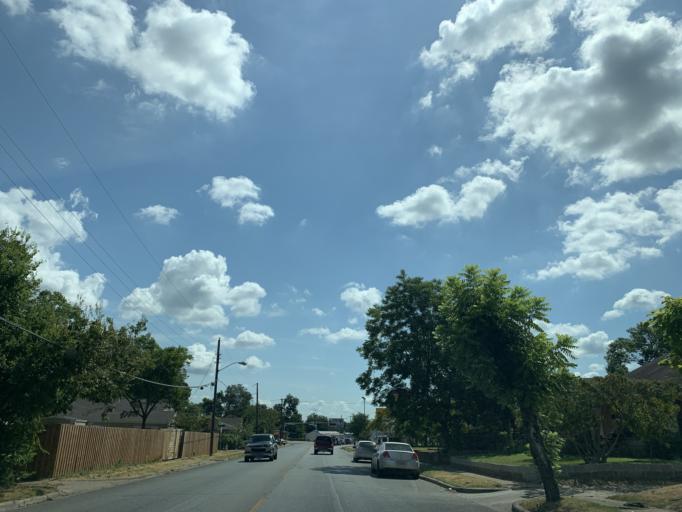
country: US
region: Texas
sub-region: Dallas County
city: Cockrell Hill
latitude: 32.7349
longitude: -96.8588
